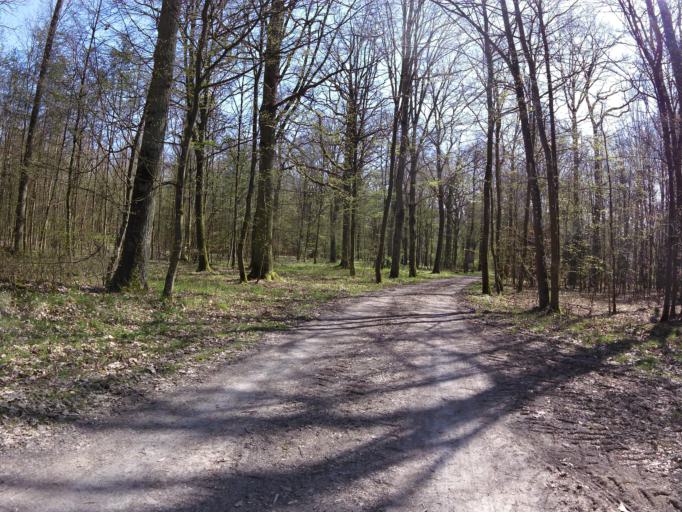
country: DE
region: Bavaria
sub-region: Regierungsbezirk Unterfranken
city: Kurnach
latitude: 49.8269
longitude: 10.0453
